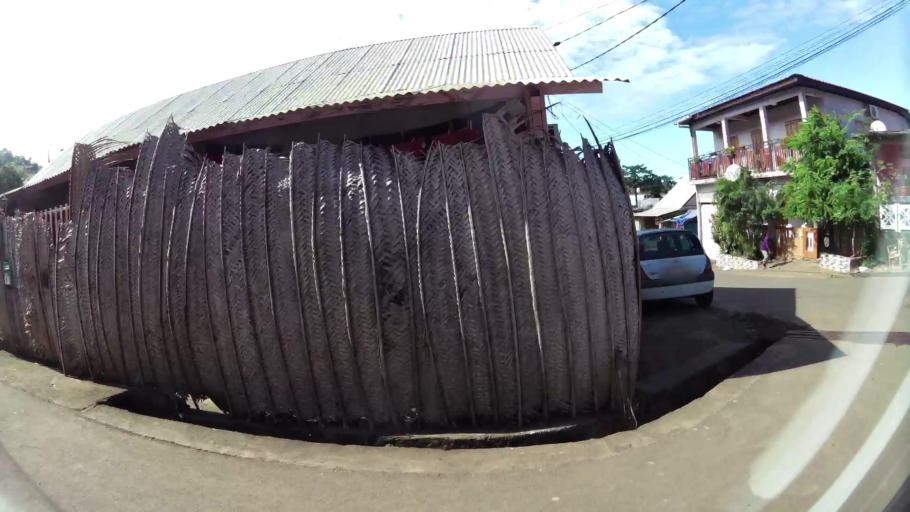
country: YT
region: Mamoudzou
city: Mamoudzou
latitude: -12.7849
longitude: 45.2193
